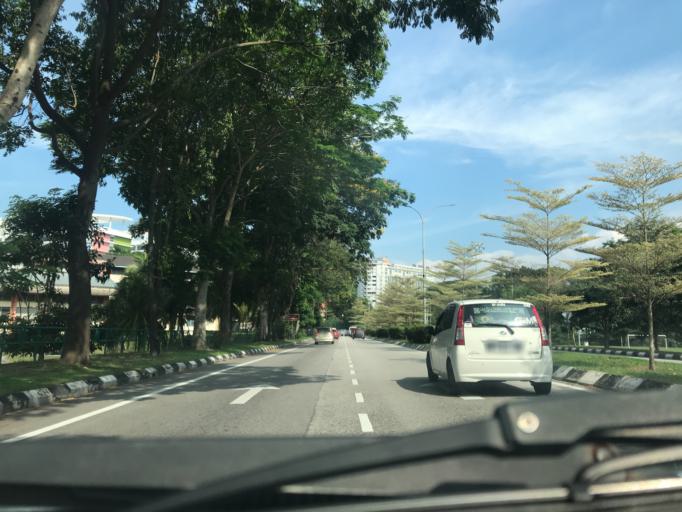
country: MY
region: Perak
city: Ipoh
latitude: 4.6052
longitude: 101.0859
